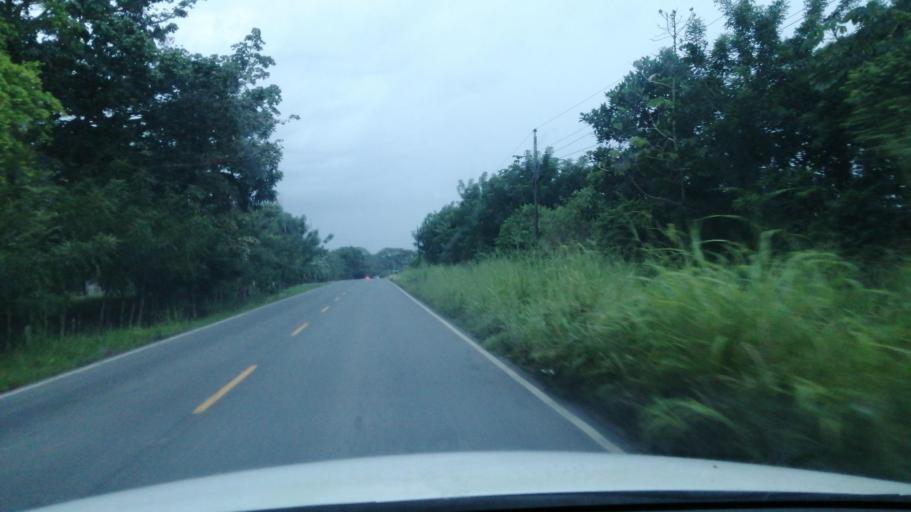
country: PA
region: Chiriqui
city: Alanje
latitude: 8.3966
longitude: -82.4893
